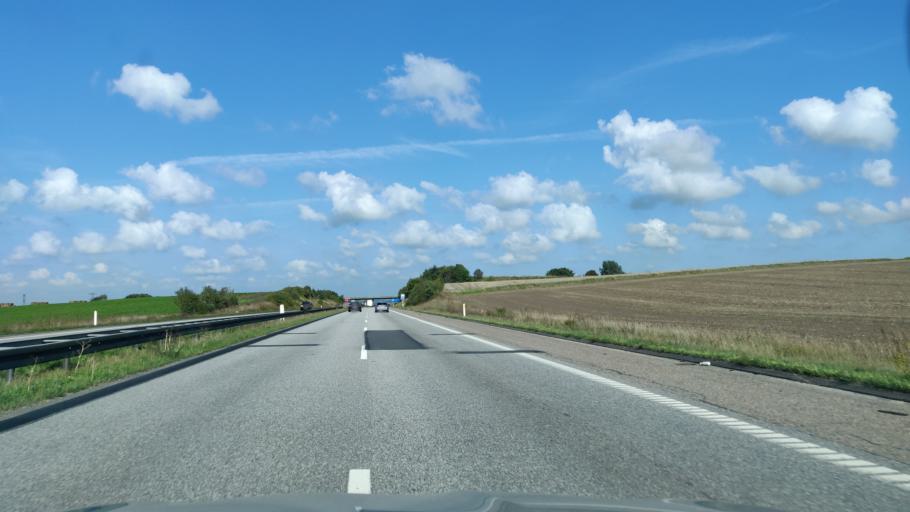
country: DK
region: North Denmark
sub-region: Alborg Kommune
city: Svenstrup
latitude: 56.9368
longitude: 9.8537
